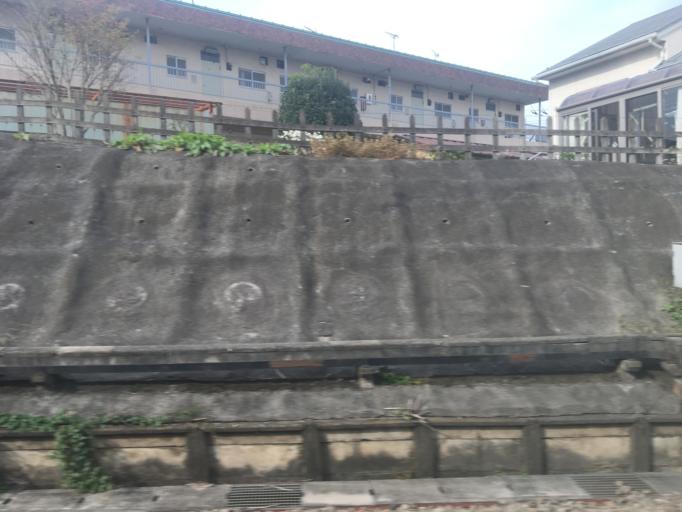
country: JP
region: Saitama
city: Sayama
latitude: 35.8550
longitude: 139.4130
